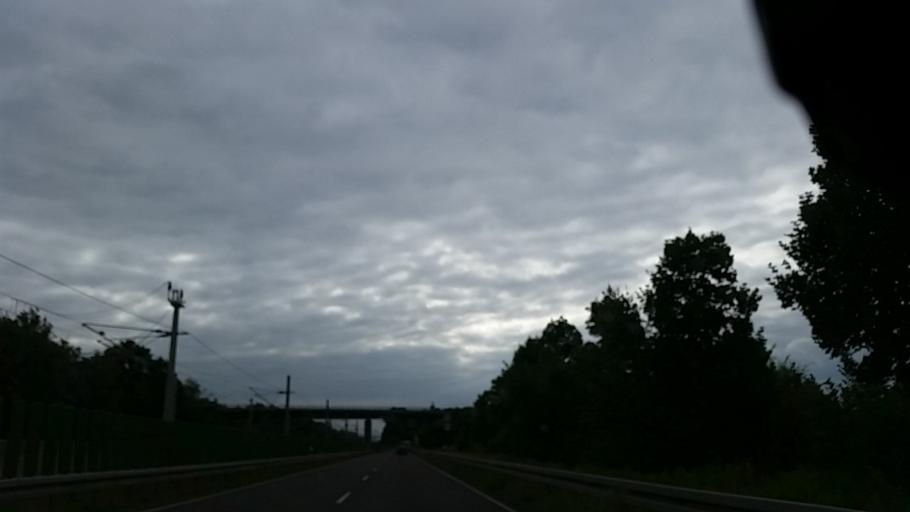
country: DE
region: Lower Saxony
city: Danndorf
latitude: 52.4314
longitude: 10.8731
